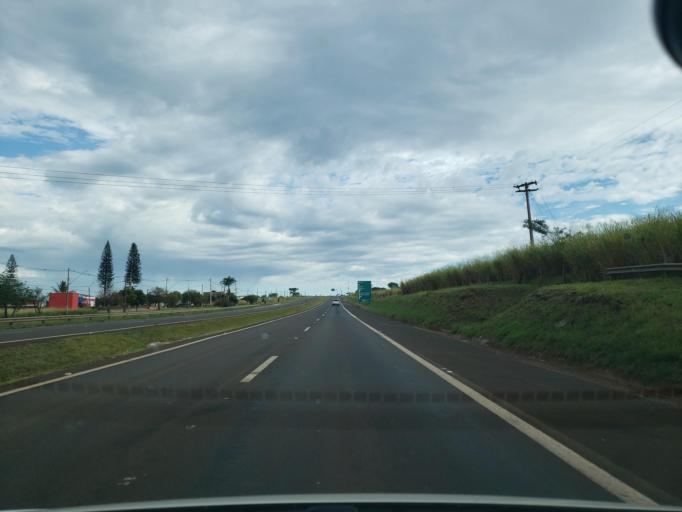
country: BR
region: Sao Paulo
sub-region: Jau
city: Jau
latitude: -22.2595
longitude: -48.5408
